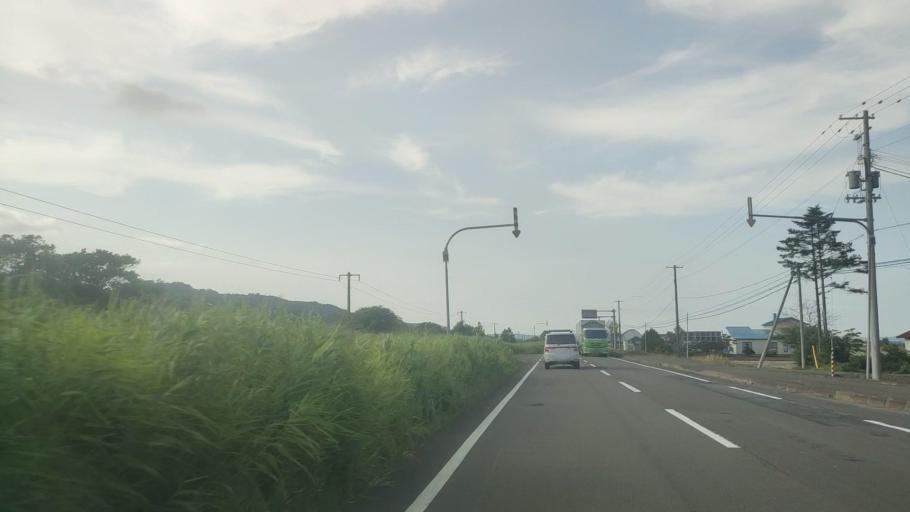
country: JP
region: Hokkaido
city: Iwamizawa
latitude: 42.9901
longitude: 141.7912
